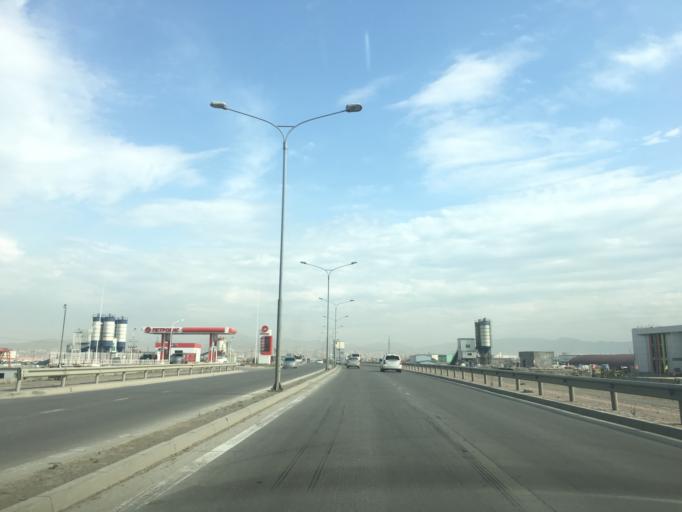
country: MN
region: Ulaanbaatar
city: Ulaanbaatar
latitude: 47.8816
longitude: 106.7847
